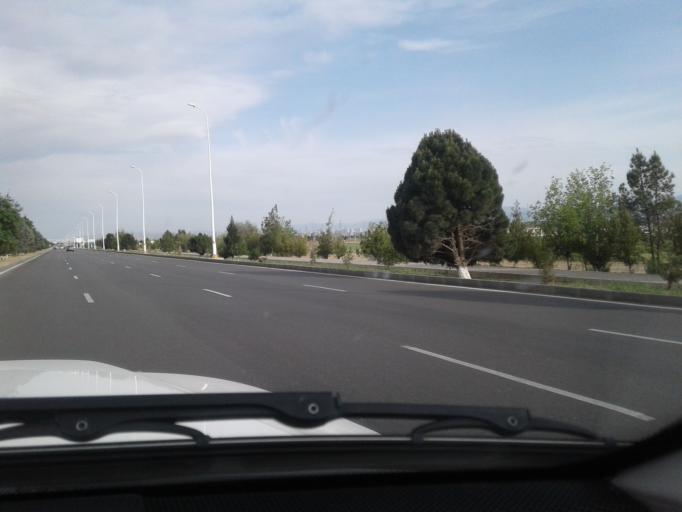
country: TM
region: Ahal
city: Ashgabat
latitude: 38.0027
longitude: 58.2948
